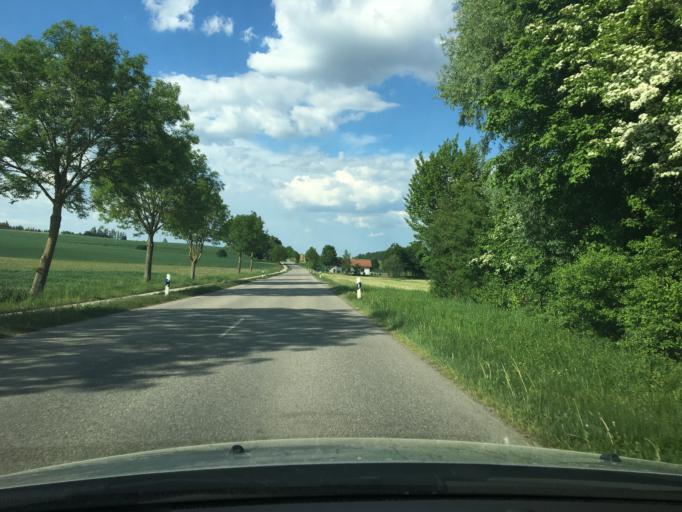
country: DE
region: Bavaria
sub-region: Lower Bavaria
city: Eching
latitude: 48.4858
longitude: 12.0550
